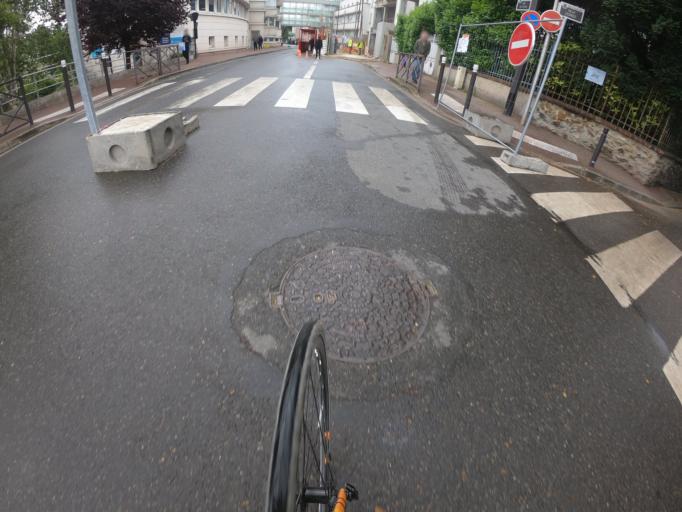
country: FR
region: Ile-de-France
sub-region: Departement des Hauts-de-Seine
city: Antony
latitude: 48.7558
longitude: 2.3019
